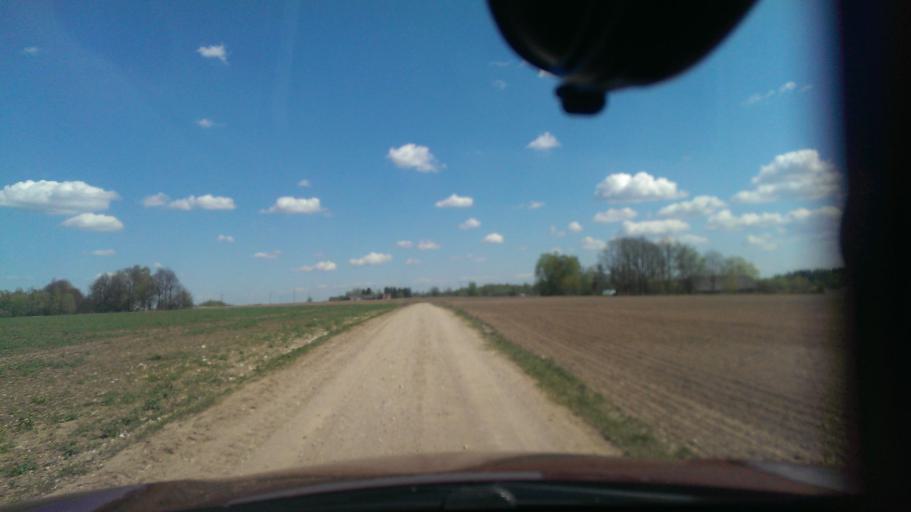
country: EE
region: Vorumaa
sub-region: Voru linn
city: Voru
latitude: 57.9523
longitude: 26.8313
